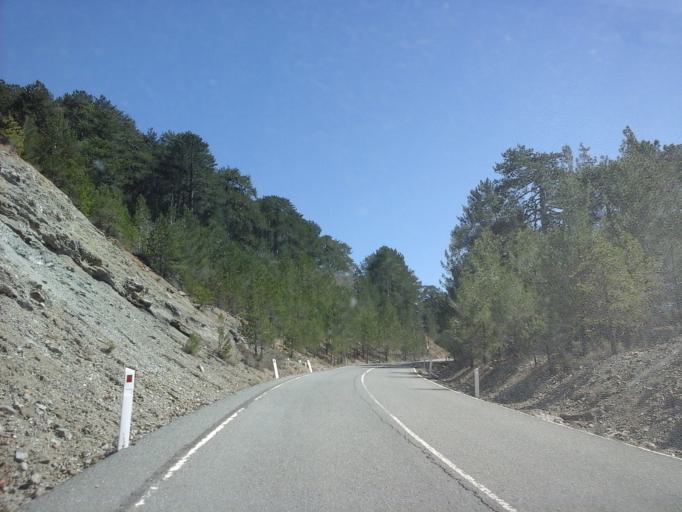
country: CY
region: Lefkosia
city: Kakopetria
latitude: 34.9102
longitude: 32.8635
